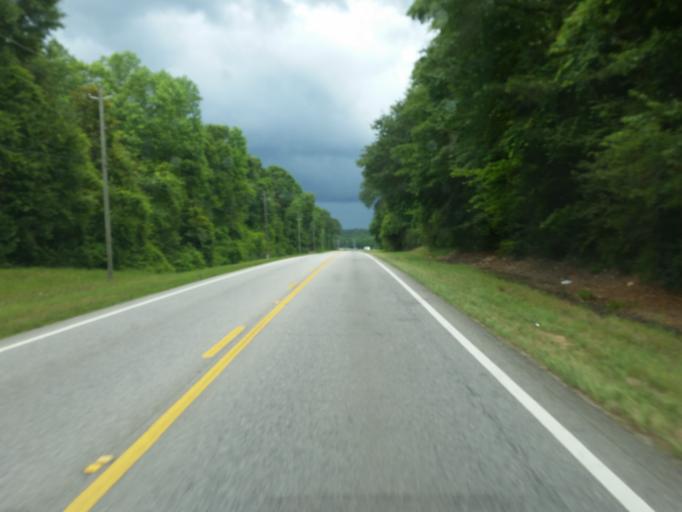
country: US
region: Mississippi
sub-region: Jackson County
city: Hurley
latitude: 30.8067
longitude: -88.3381
